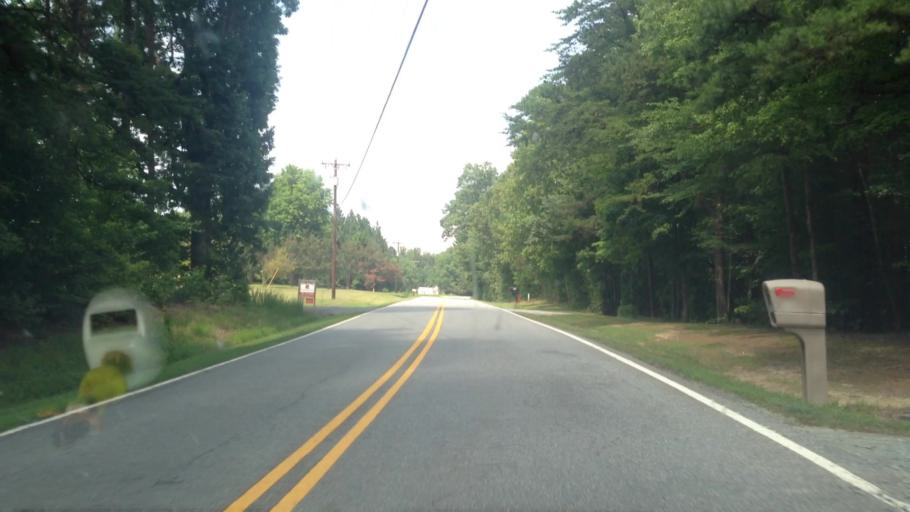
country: US
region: North Carolina
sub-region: Forsyth County
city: Walkertown
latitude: 36.2305
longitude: -80.1110
